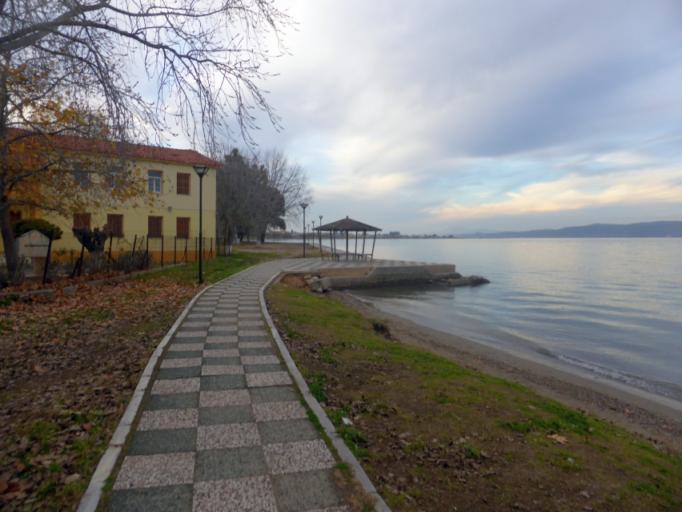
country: GR
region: Attica
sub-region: Nomarchia Anatolikis Attikis
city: Skala Oropou
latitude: 38.3221
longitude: 23.7866
